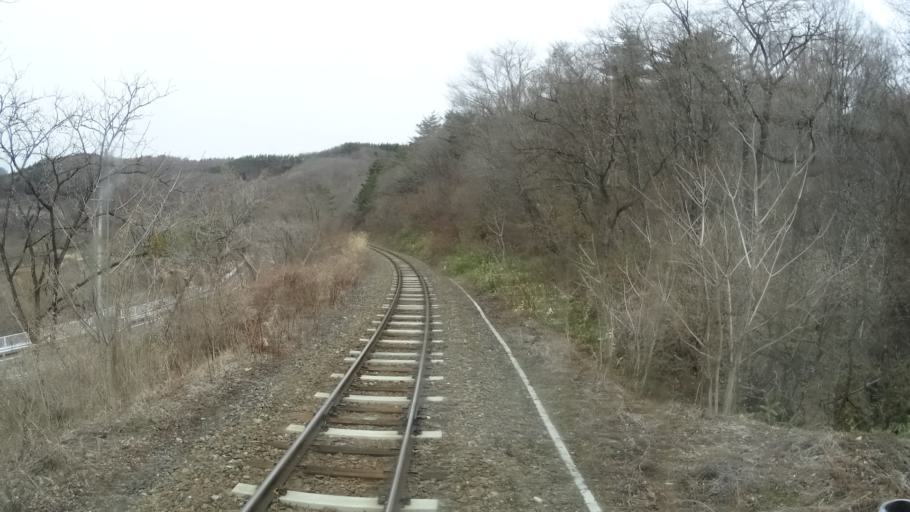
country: JP
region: Iwate
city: Tono
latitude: 39.3081
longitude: 141.3800
